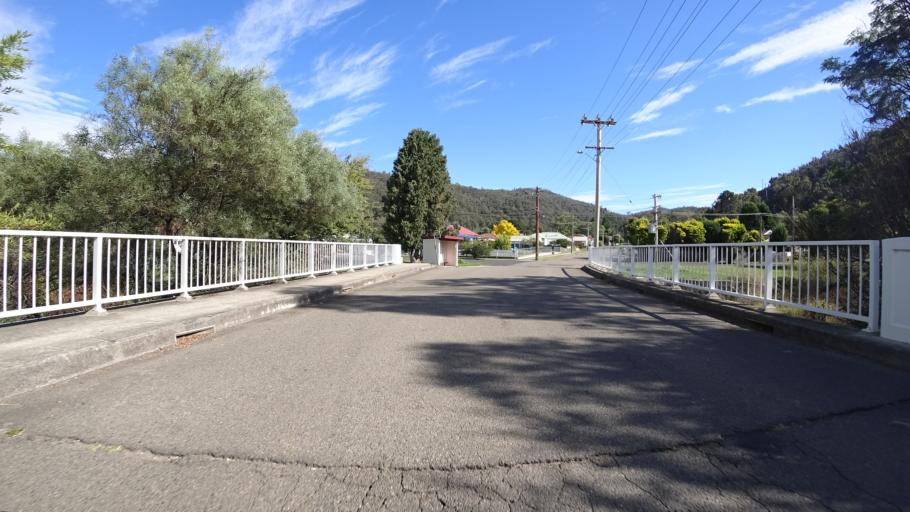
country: AU
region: New South Wales
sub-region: Lithgow
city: Lithgow
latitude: -33.4718
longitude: 150.1691
